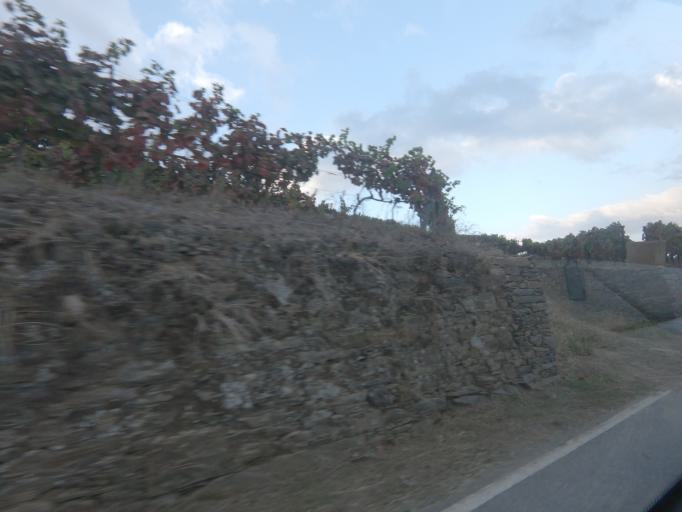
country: PT
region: Vila Real
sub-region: Mesao Frio
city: Mesao Frio
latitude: 41.1723
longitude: -7.8727
